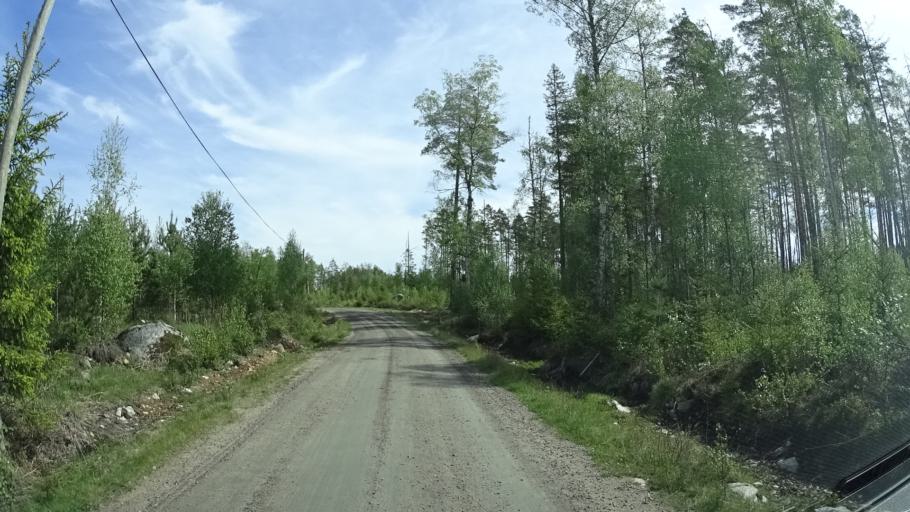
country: SE
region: OEstergoetland
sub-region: Finspangs Kommun
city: Finspang
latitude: 58.7778
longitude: 15.8540
